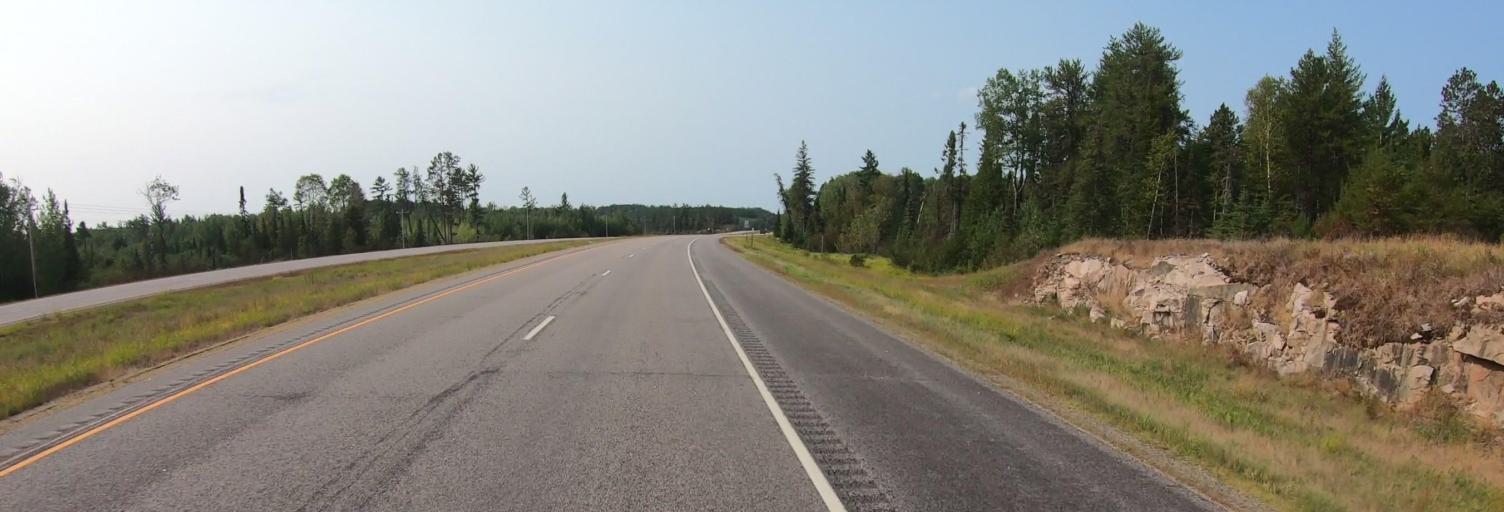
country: US
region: Minnesota
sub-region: Saint Louis County
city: Mountain Iron
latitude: 47.7030
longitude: -92.6442
